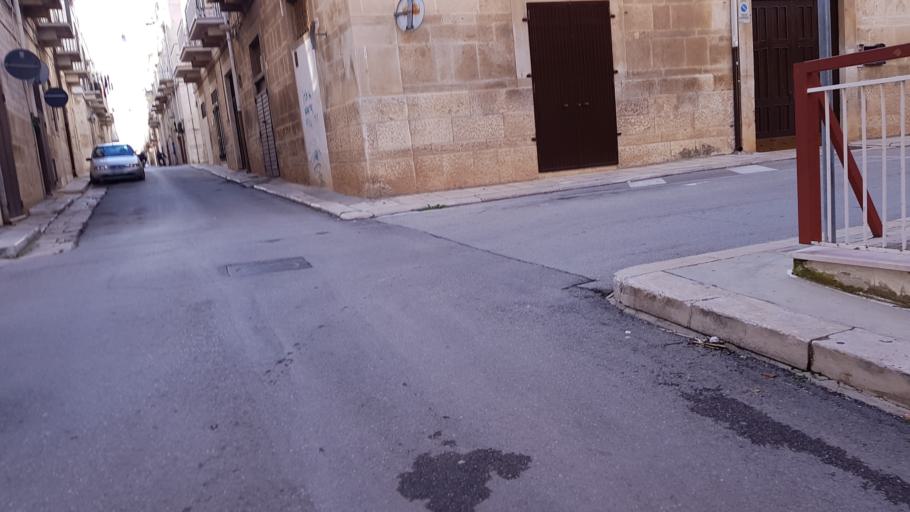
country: IT
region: Apulia
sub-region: Provincia di Bari
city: Ruvo di Puglia
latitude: 41.1189
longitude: 16.4879
